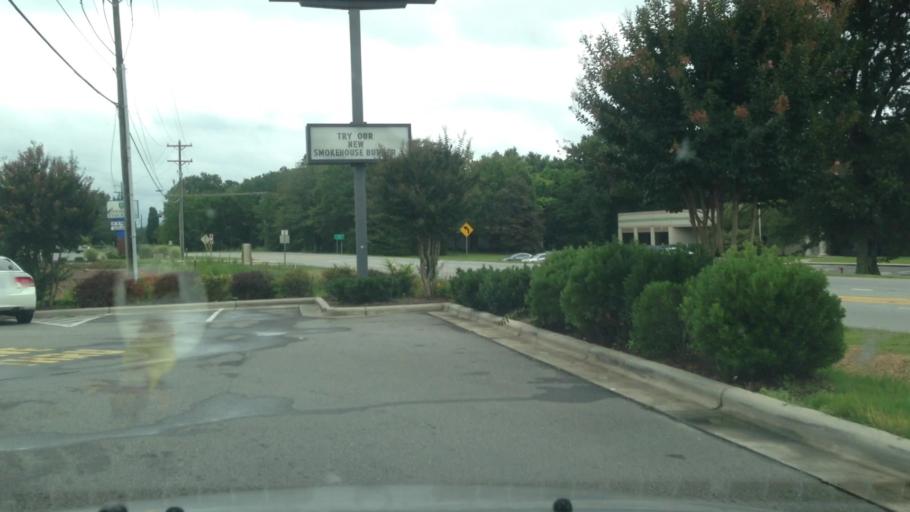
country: US
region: North Carolina
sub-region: Rockingham County
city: Mayodan
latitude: 36.4175
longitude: -79.9341
